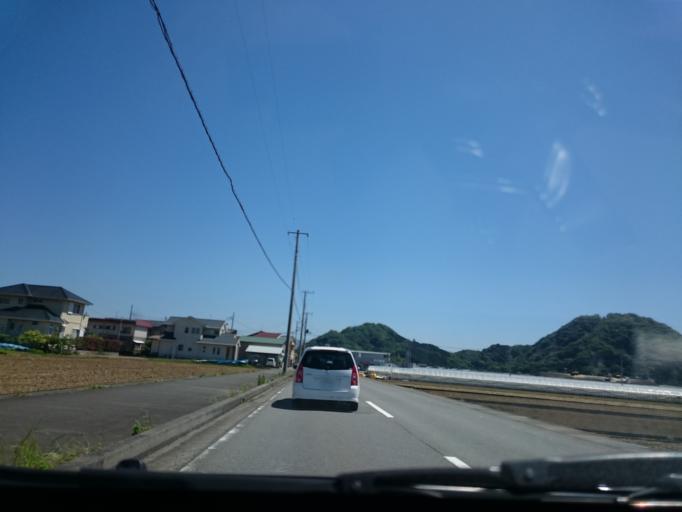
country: JP
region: Shizuoka
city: Mishima
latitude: 35.0775
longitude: 138.9288
